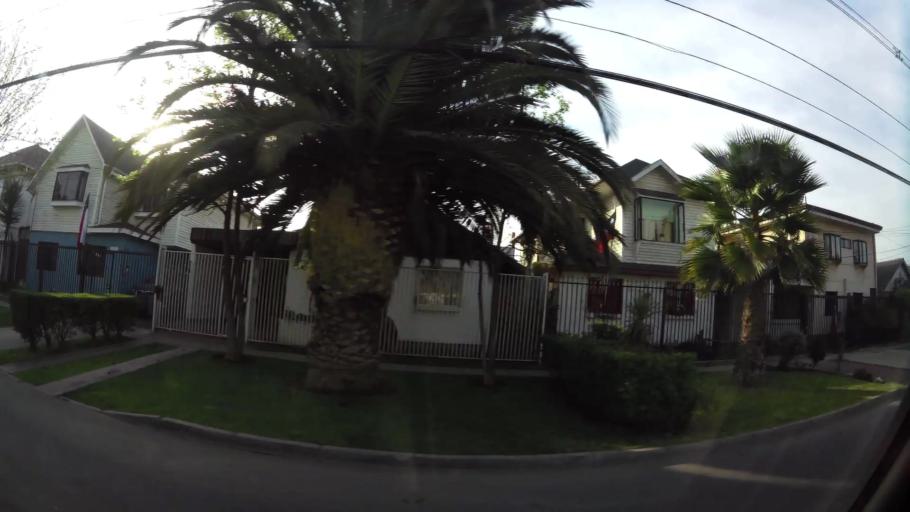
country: CL
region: Santiago Metropolitan
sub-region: Provincia de Maipo
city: San Bernardo
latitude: -33.5592
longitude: -70.7846
